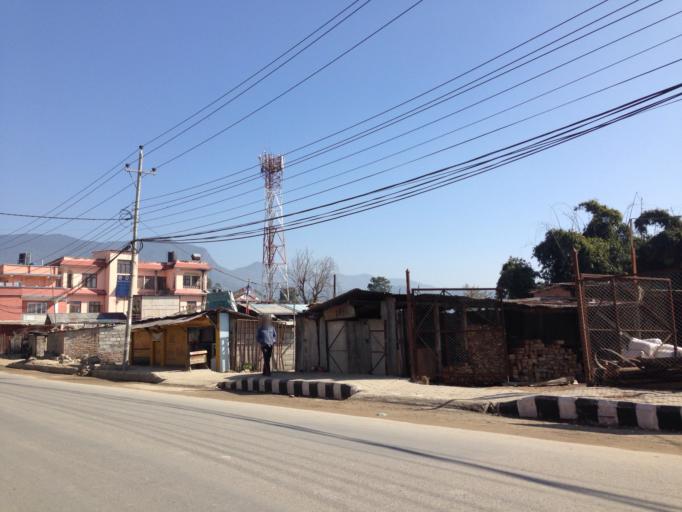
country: NP
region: Central Region
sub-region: Bagmati Zone
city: Kathmandu
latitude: 27.7541
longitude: 85.3478
